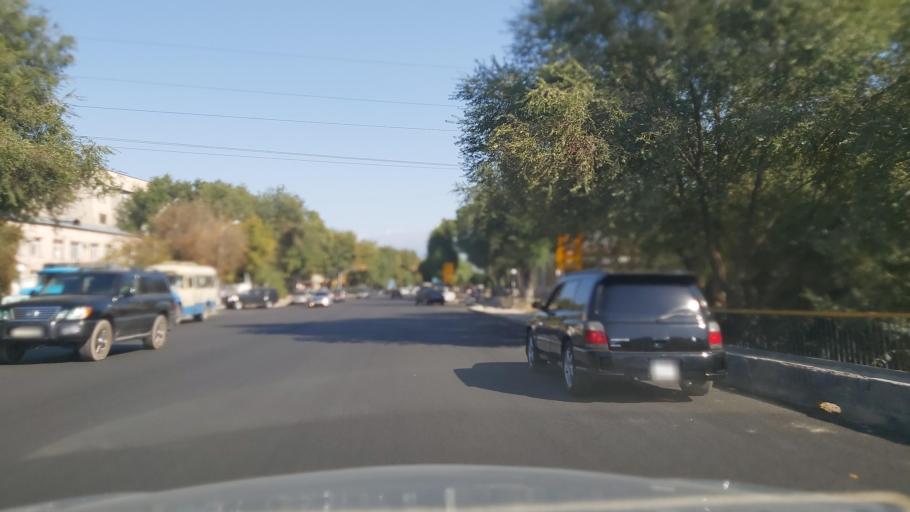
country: KZ
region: Almaty Oblysy
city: Pervomayskiy
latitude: 43.3243
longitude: 76.9092
